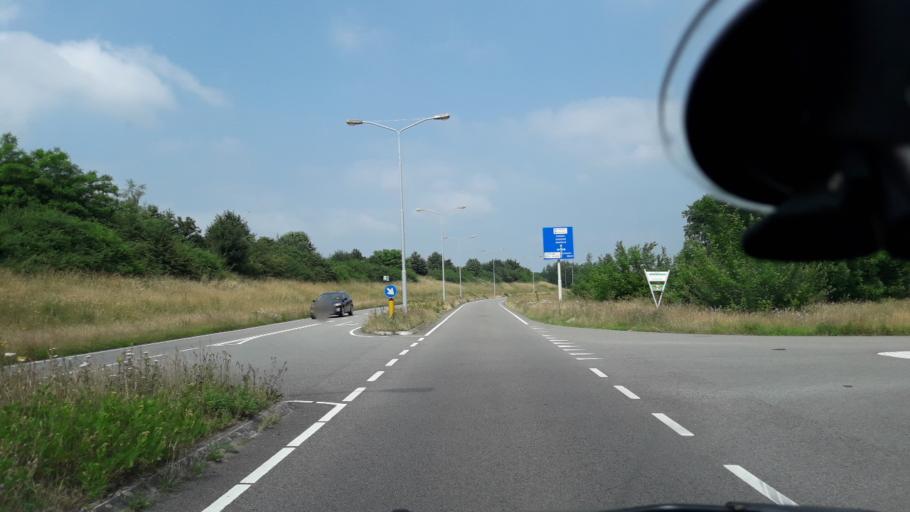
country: NL
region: Gelderland
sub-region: Gemeente Harderwijk
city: Harderwijk
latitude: 52.3217
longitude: 5.6077
